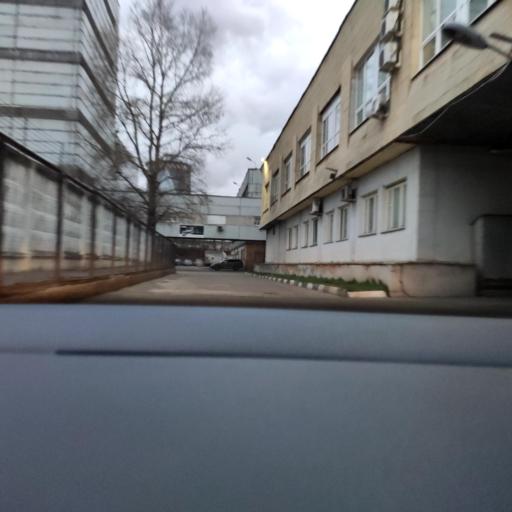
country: RU
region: Moscow
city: Metrogorodok
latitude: 55.8196
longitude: 37.7798
